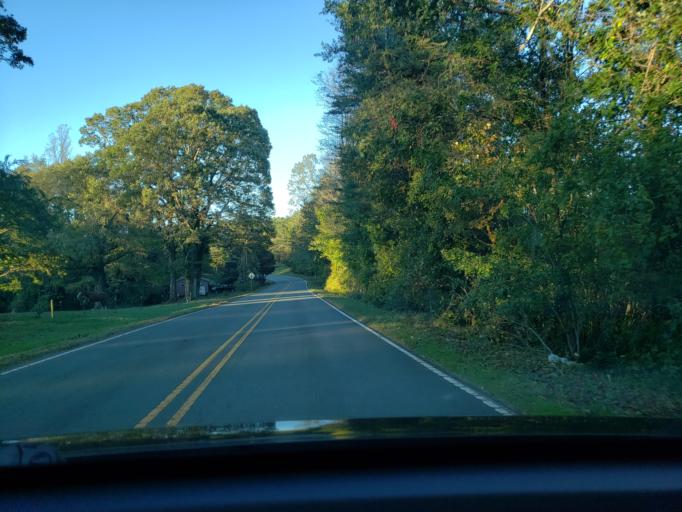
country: US
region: North Carolina
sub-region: Forsyth County
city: Walkertown
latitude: 36.2263
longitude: -80.1987
